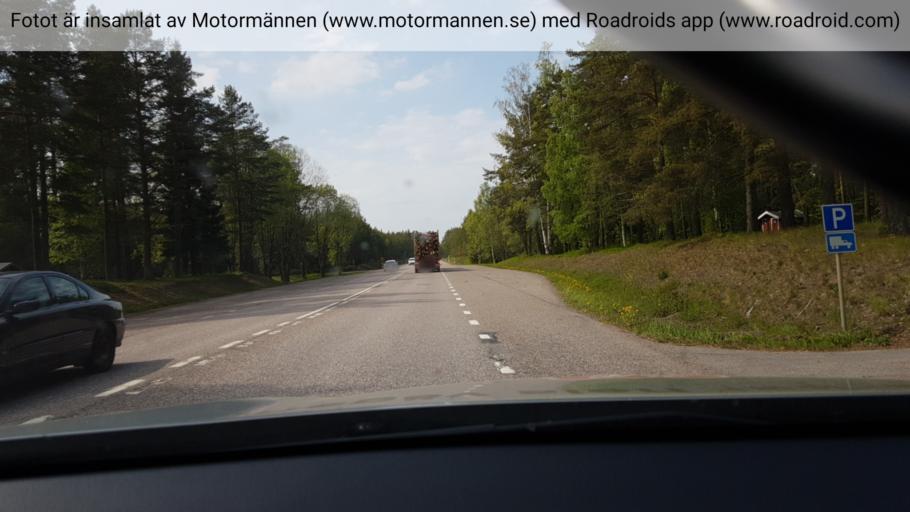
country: SE
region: Uppsala
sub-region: Alvkarleby Kommun
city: AElvkarleby
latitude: 60.6035
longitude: 17.4480
